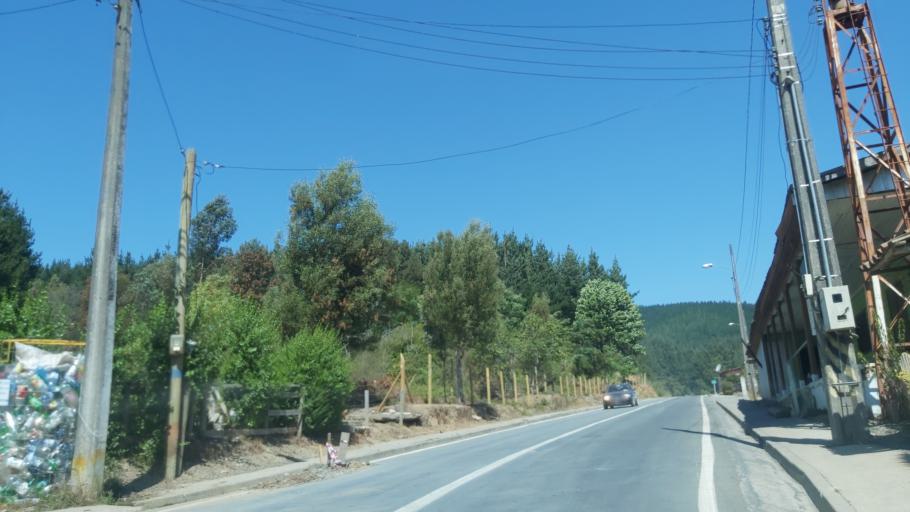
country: CL
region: Biobio
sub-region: Provincia de Concepcion
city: Tome
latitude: -36.5551
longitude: -72.8648
